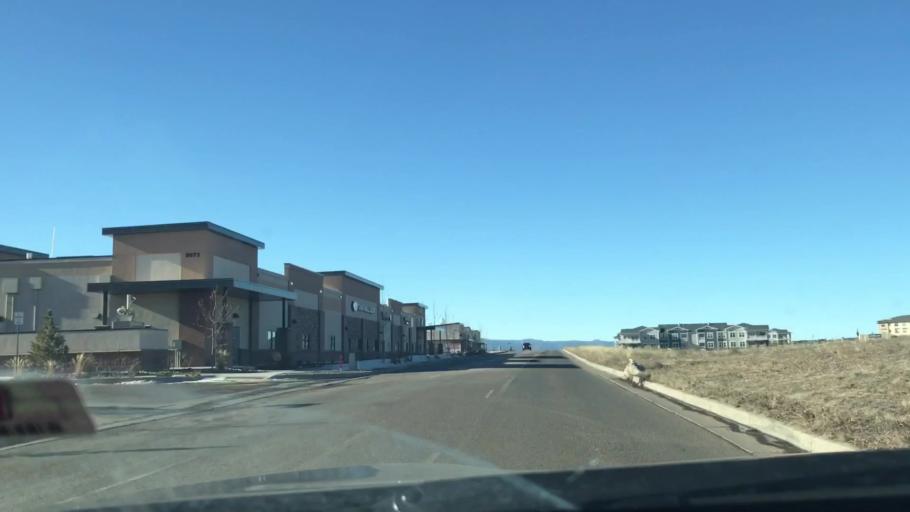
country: US
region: Colorado
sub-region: El Paso County
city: Black Forest
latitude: 38.9710
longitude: -104.7413
